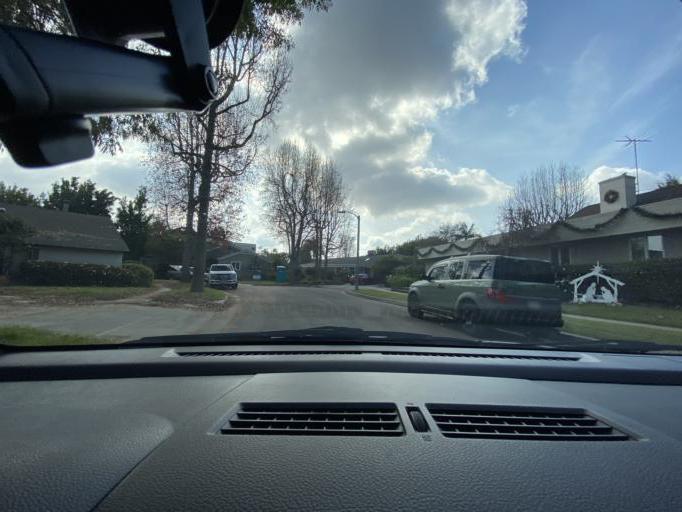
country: US
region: California
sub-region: Los Angeles County
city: Culver City
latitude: 34.0197
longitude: -118.4329
